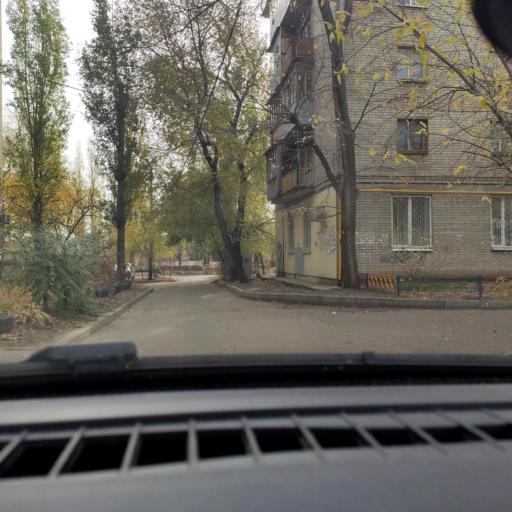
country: RU
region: Voronezj
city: Voronezh
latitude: 51.6466
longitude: 39.1509
